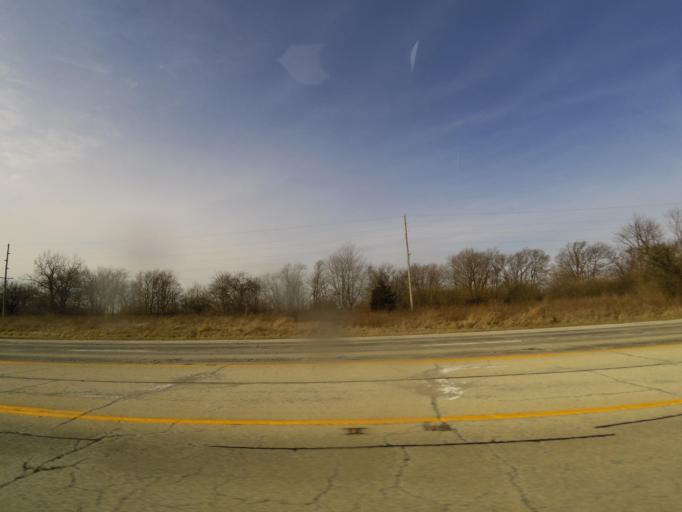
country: US
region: Illinois
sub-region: Macon County
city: Macon
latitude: 39.7731
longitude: -88.9809
